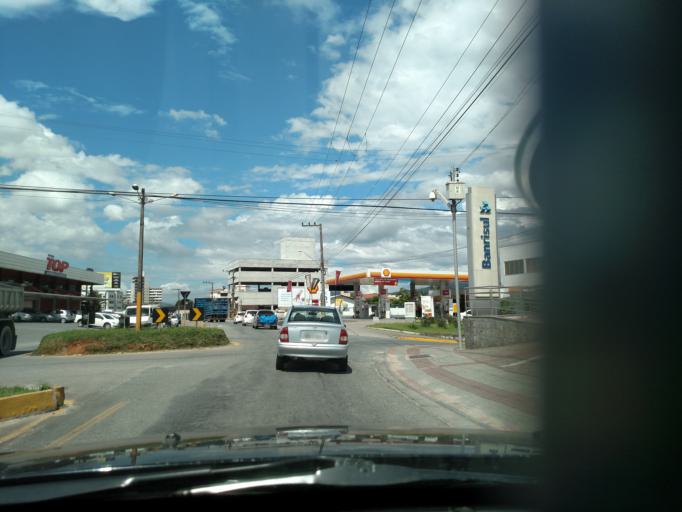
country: BR
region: Santa Catarina
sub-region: Gaspar
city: Gaspar
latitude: -26.9308
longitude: -48.9503
